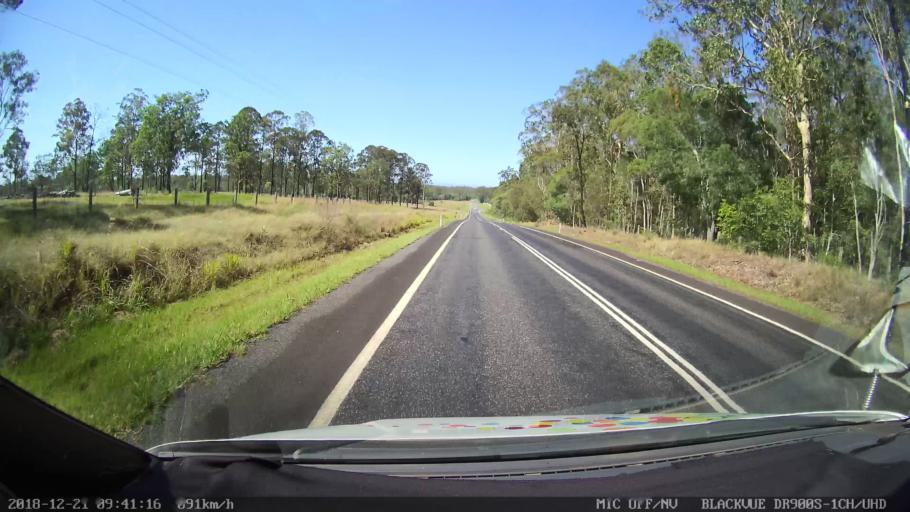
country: AU
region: New South Wales
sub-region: Clarence Valley
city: Grafton
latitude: -29.5831
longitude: 152.9589
